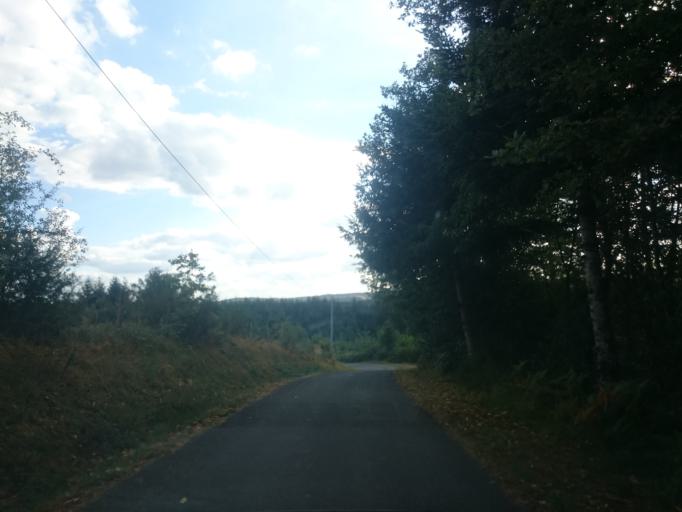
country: FR
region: Auvergne
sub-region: Departement du Cantal
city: Saint-Mamet-la-Salvetat
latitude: 44.8612
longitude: 2.2505
